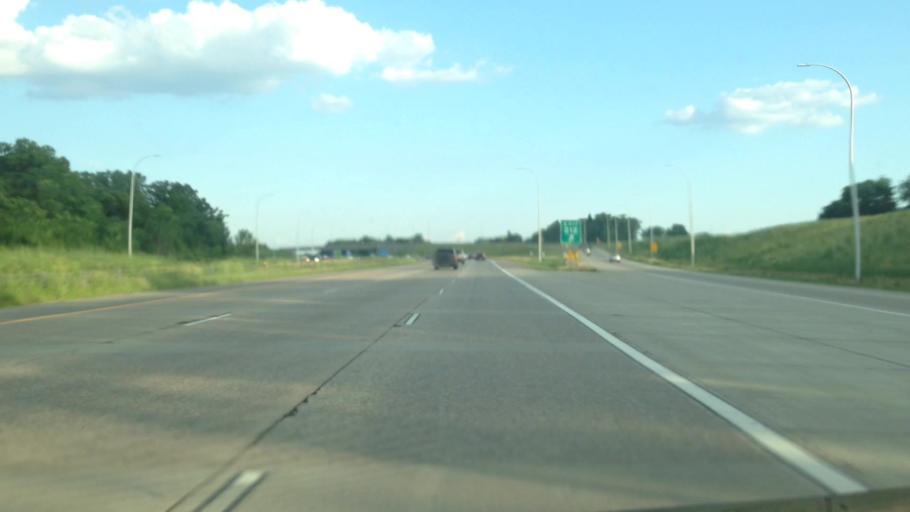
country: US
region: Minnesota
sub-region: Hennepin County
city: Corcoran
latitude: 45.1439
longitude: -93.4986
